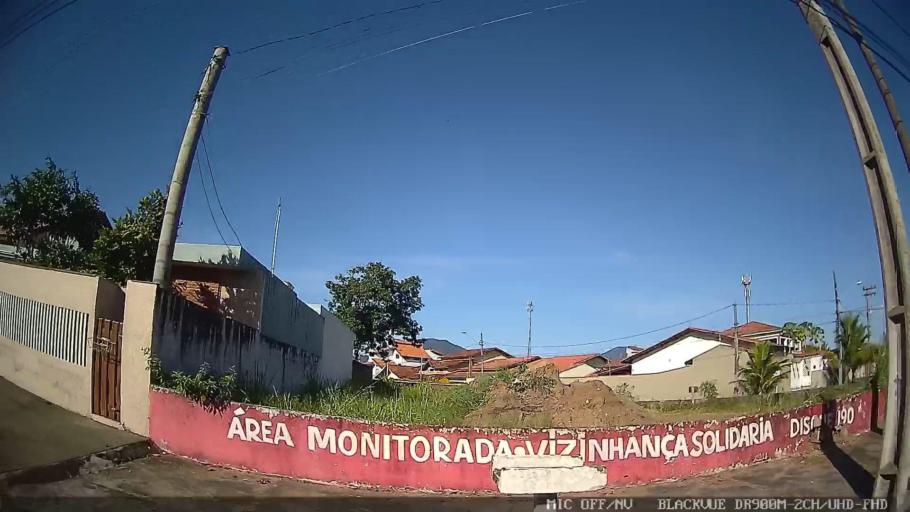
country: BR
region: Sao Paulo
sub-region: Peruibe
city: Peruibe
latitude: -24.3025
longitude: -46.9789
